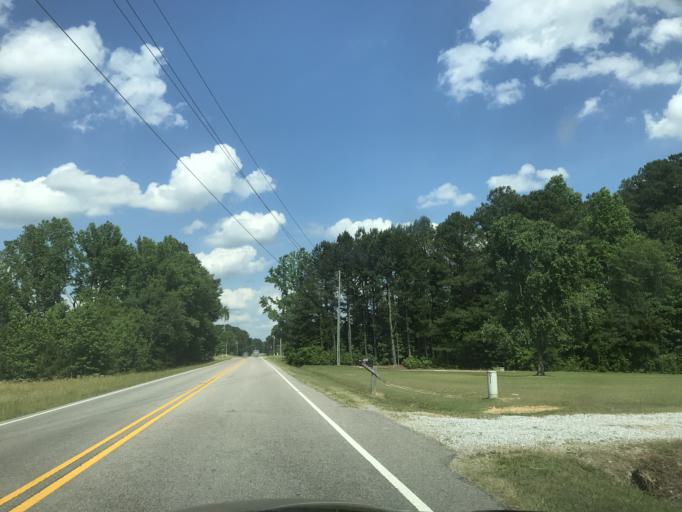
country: US
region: North Carolina
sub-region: Wake County
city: Rolesville
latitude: 35.9734
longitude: -78.3756
